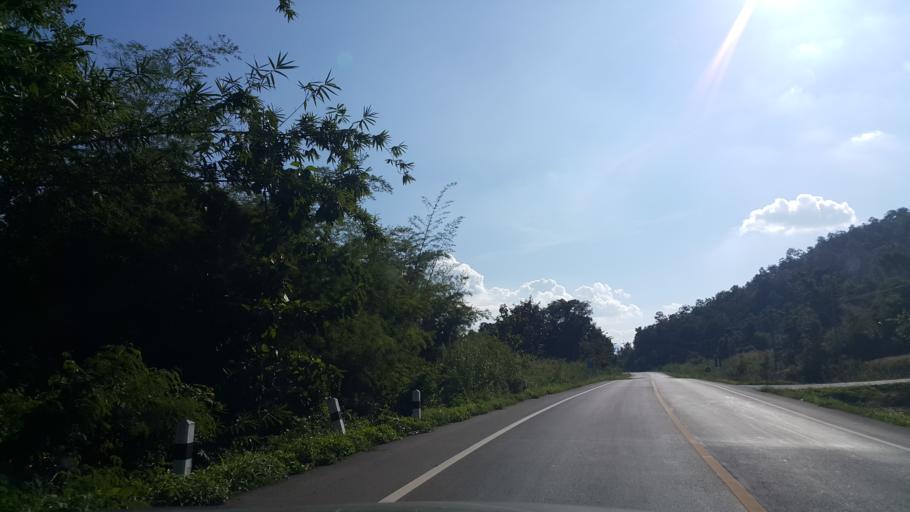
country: TH
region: Lamphun
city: Mae Tha
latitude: 18.4883
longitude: 99.1827
